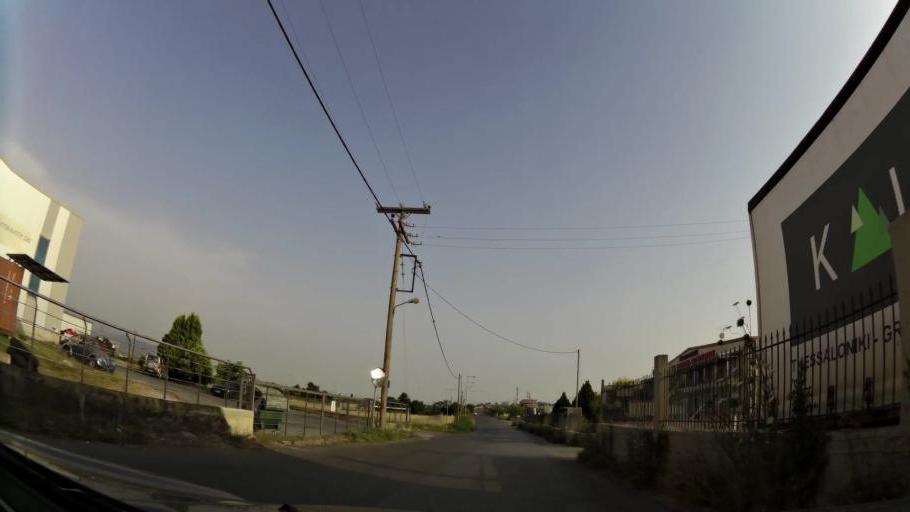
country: GR
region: Central Macedonia
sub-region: Nomos Thessalonikis
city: Evosmos
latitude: 40.6993
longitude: 22.9094
